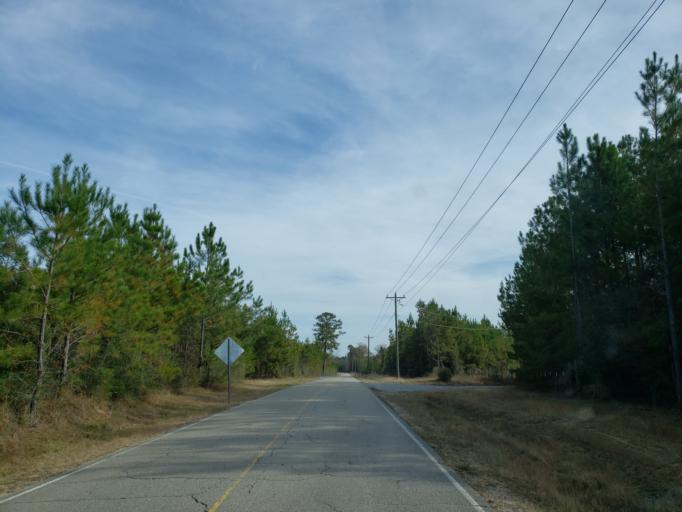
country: US
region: Mississippi
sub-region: Forrest County
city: Rawls Springs
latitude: 31.4187
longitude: -89.4236
